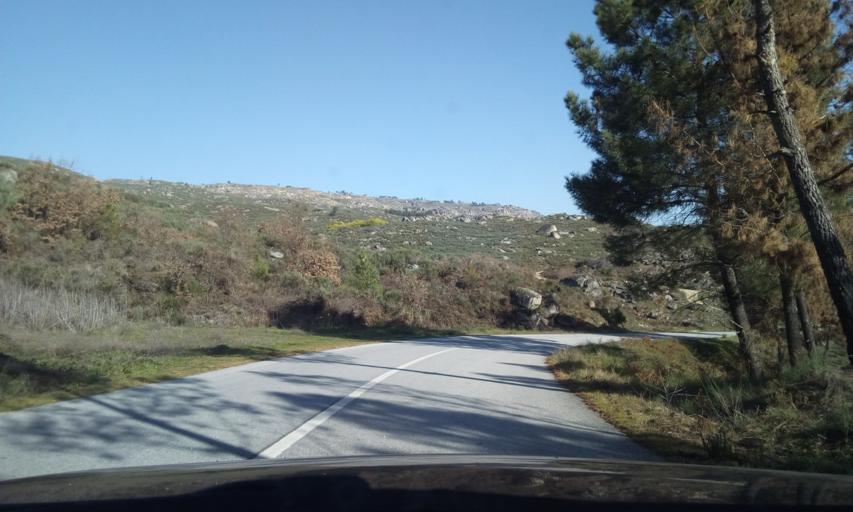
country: PT
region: Guarda
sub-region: Fornos de Algodres
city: Fornos de Algodres
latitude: 40.6456
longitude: -7.4726
